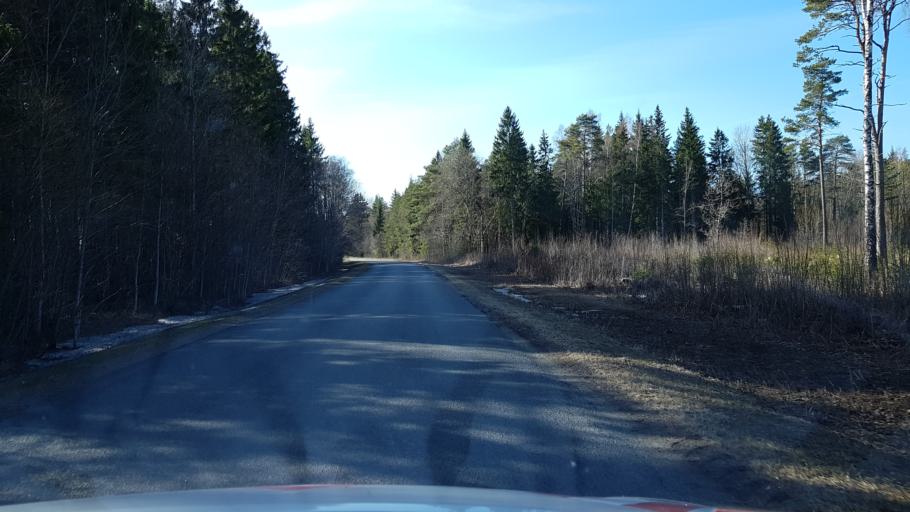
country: EE
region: Harju
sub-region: Nissi vald
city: Riisipere
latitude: 59.0983
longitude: 24.3314
